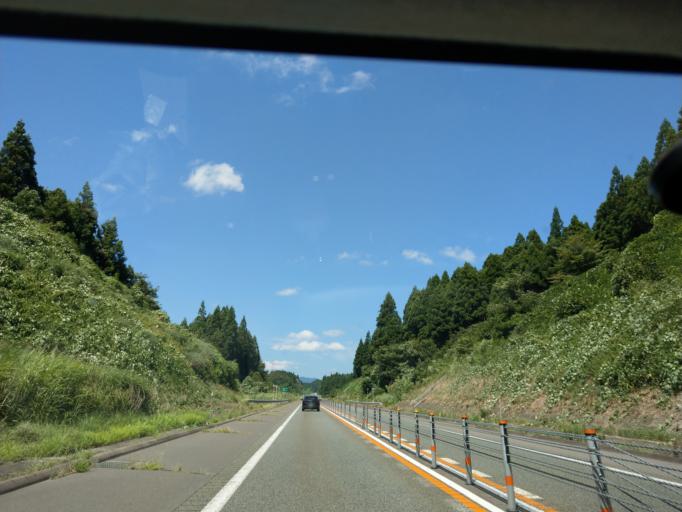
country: JP
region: Akita
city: Akita
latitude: 39.6895
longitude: 140.1857
